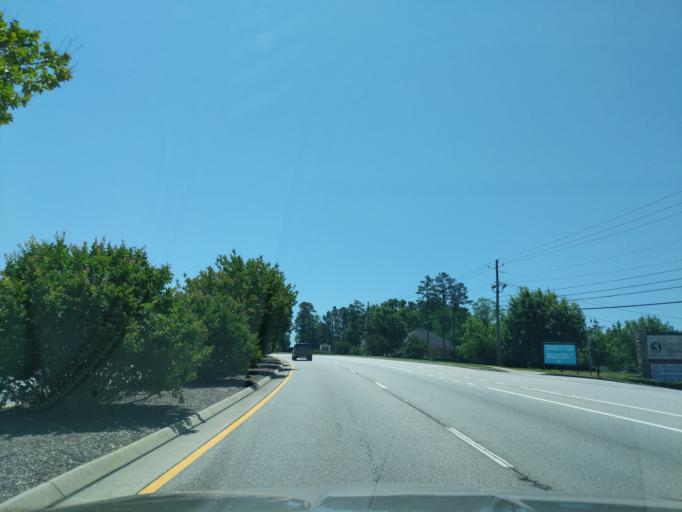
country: US
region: Georgia
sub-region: Columbia County
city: Martinez
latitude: 33.5339
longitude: -82.0778
